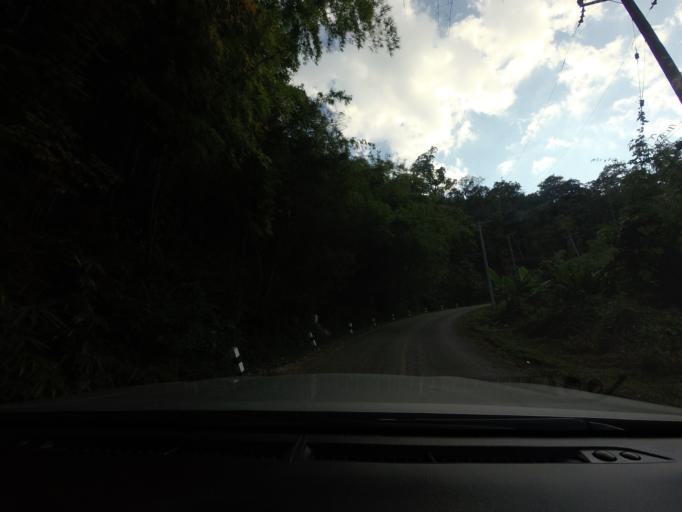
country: TH
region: Chiang Mai
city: Phrao
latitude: 19.5068
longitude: 99.1712
